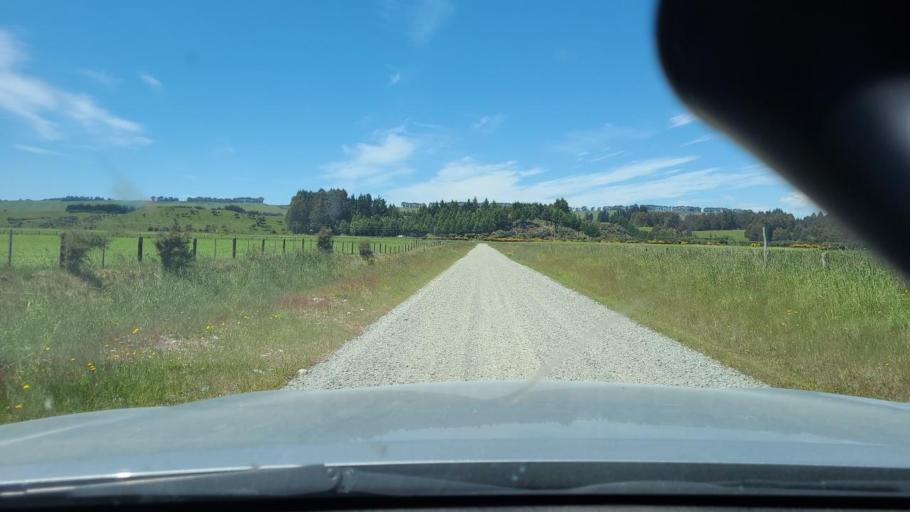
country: NZ
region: Southland
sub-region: Southland District
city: Te Anau
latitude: -45.4715
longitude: 167.6944
